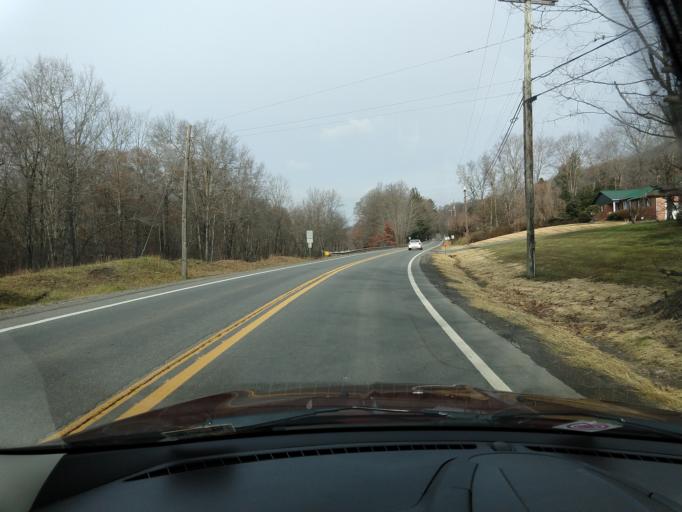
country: US
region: West Virginia
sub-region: Greenbrier County
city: Rainelle
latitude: 37.9649
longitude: -80.6982
